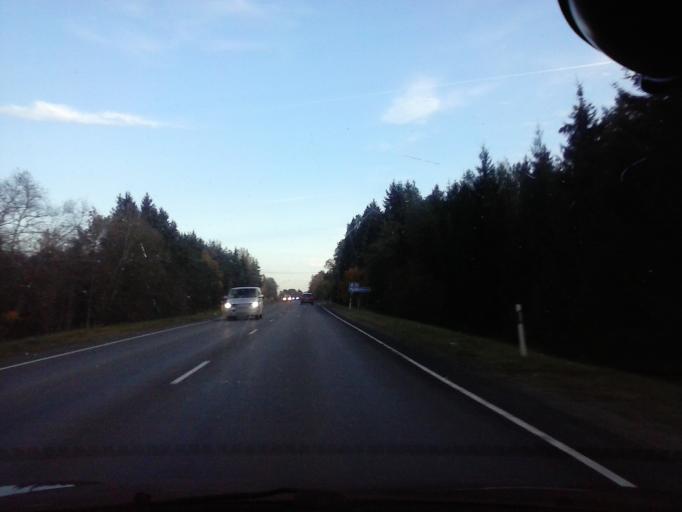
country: EE
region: Harju
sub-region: Nissi vald
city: Turba
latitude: 58.9356
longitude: 24.0948
